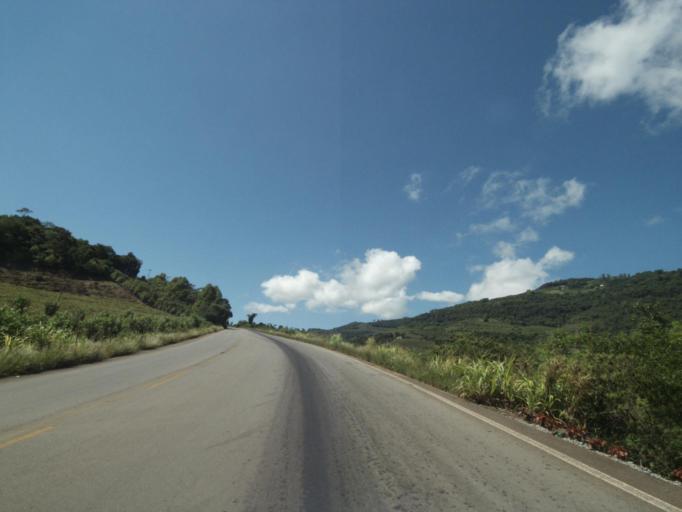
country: BR
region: Rio Grande do Sul
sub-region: Bento Goncalves
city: Bento Goncalves
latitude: -29.0980
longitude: -51.6272
